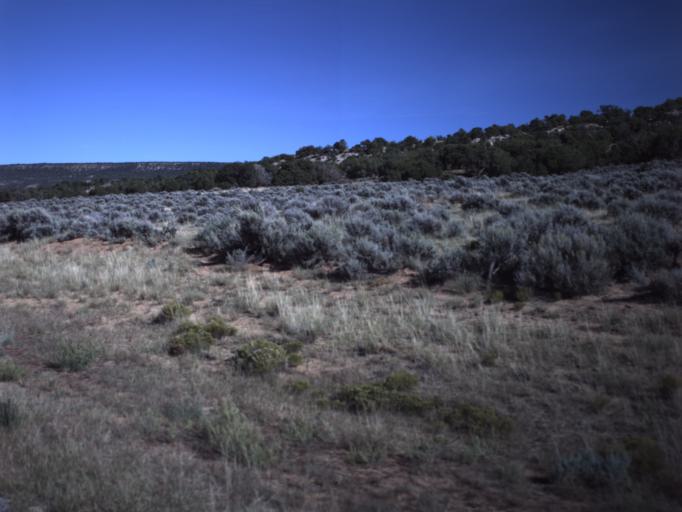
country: US
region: Utah
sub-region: San Juan County
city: Monticello
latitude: 38.0000
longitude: -109.4666
